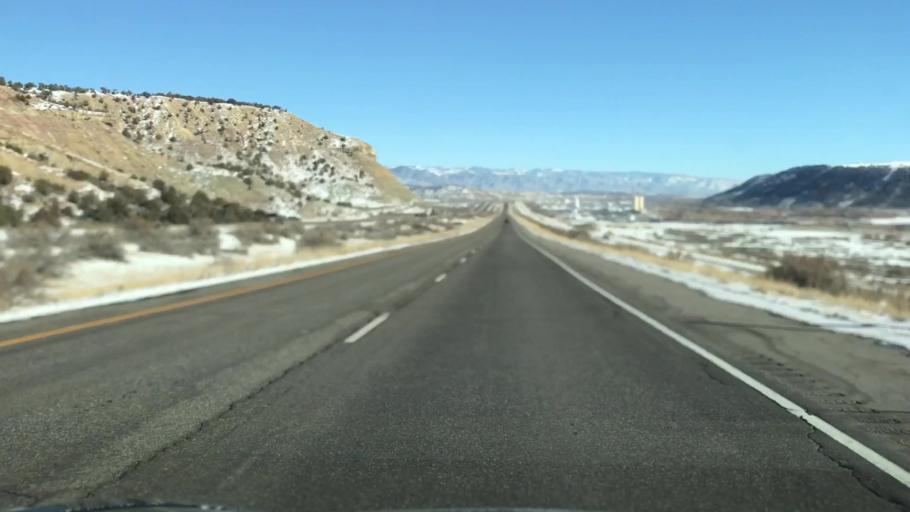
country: US
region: Colorado
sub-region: Garfield County
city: Rifle
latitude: 39.5099
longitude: -107.8754
